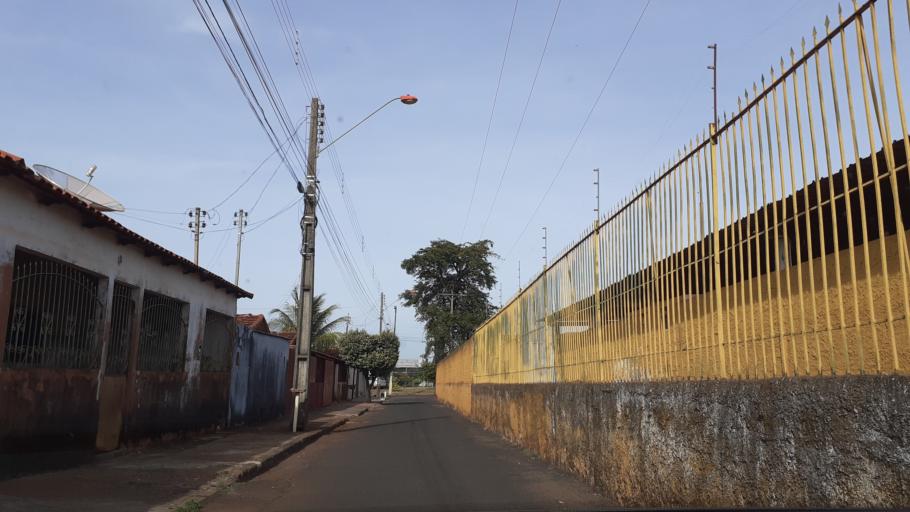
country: BR
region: Goias
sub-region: Itumbiara
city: Itumbiara
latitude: -18.4155
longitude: -49.2404
